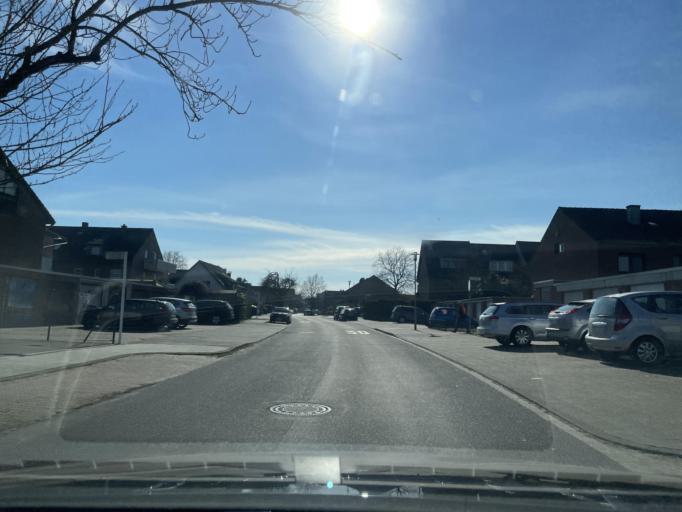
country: DE
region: North Rhine-Westphalia
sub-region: Regierungsbezirk Dusseldorf
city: Monchengladbach
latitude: 51.2284
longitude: 6.4490
